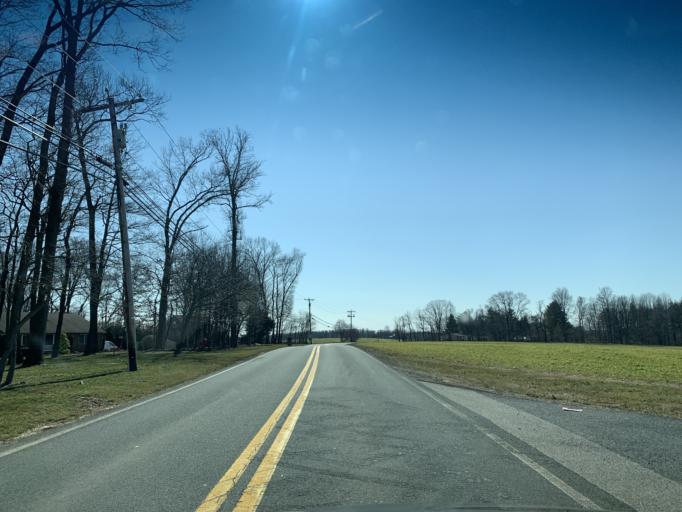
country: US
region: Maryland
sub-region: Carroll County
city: Hampstead
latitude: 39.5795
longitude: -76.8731
